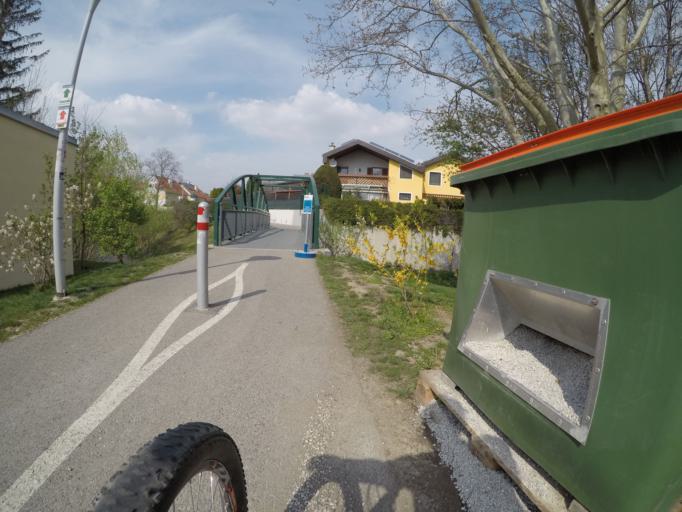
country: AT
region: Lower Austria
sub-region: Politischer Bezirk Modling
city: Wiener Neudorf
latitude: 48.0841
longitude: 16.3095
